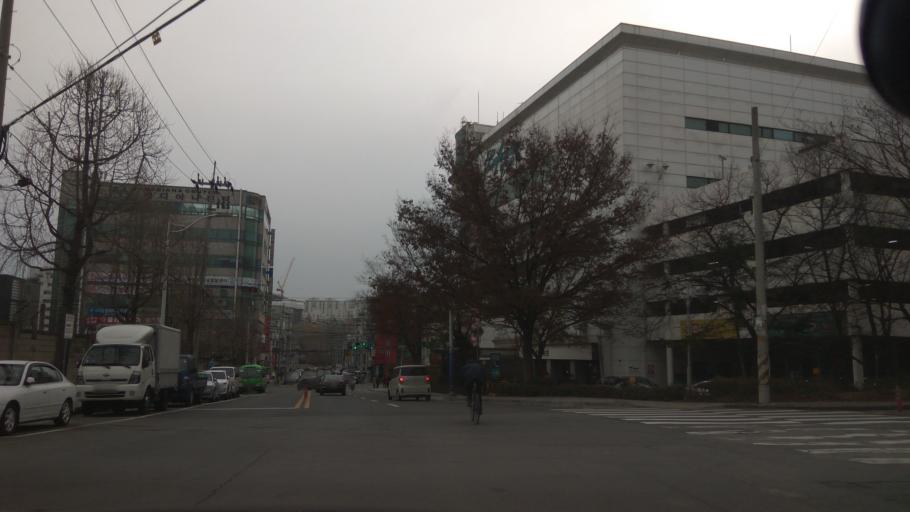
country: KR
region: Incheon
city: Incheon
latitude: 37.4914
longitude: 126.7108
